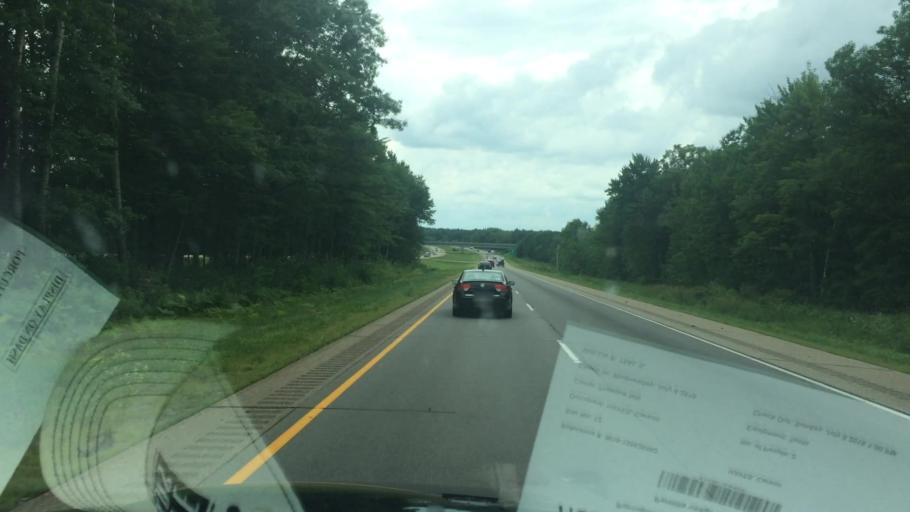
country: US
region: Wisconsin
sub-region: Marathon County
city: Mosinee
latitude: 44.7085
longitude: -89.6560
